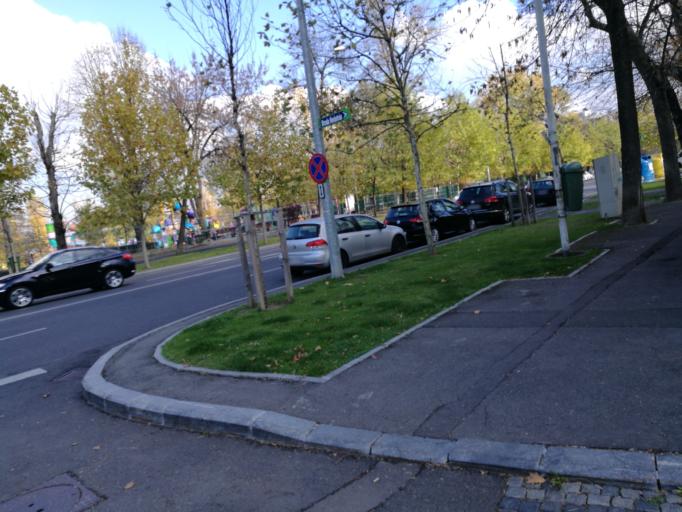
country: RO
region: Bucuresti
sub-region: Municipiul Bucuresti
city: Bucharest
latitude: 44.4707
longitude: 26.0889
